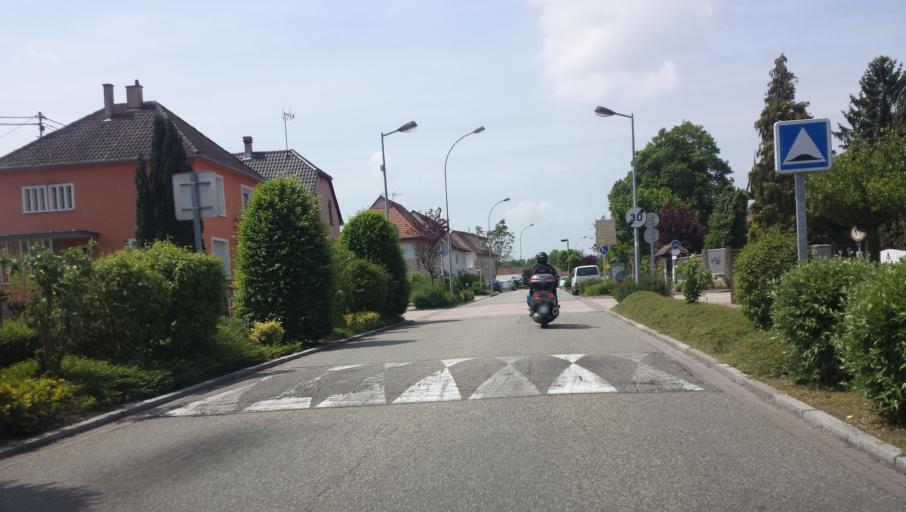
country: DE
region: Rheinland-Pfalz
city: Berg
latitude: 48.9754
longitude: 8.1717
